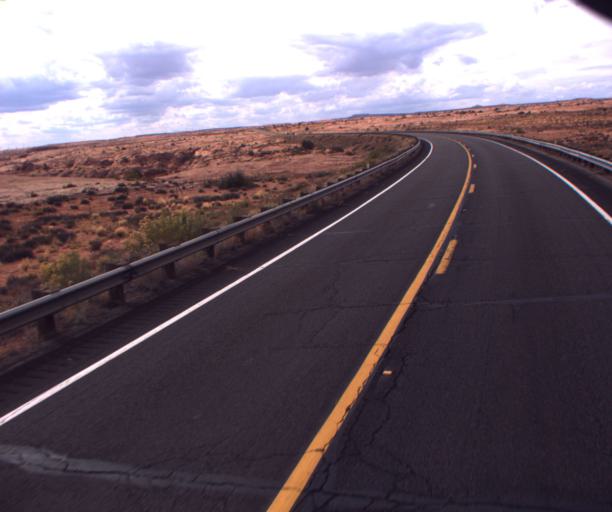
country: US
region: Arizona
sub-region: Navajo County
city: Kayenta
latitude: 36.9464
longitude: -109.7199
